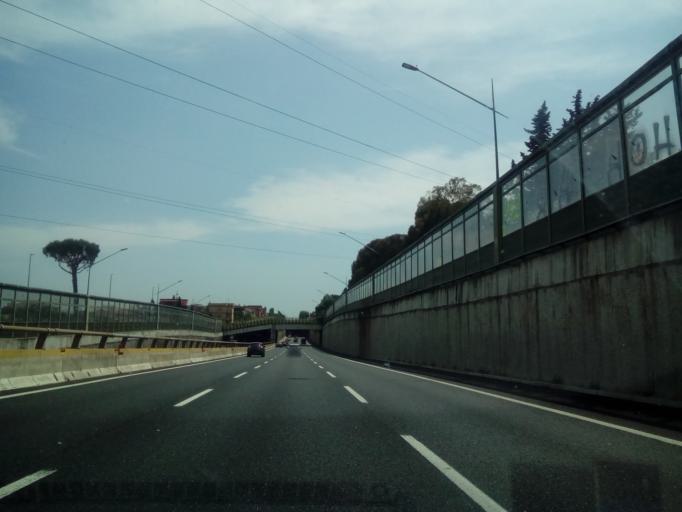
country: IT
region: Latium
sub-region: Citta metropolitana di Roma Capitale
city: Valle Santa
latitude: 41.9506
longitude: 12.3828
